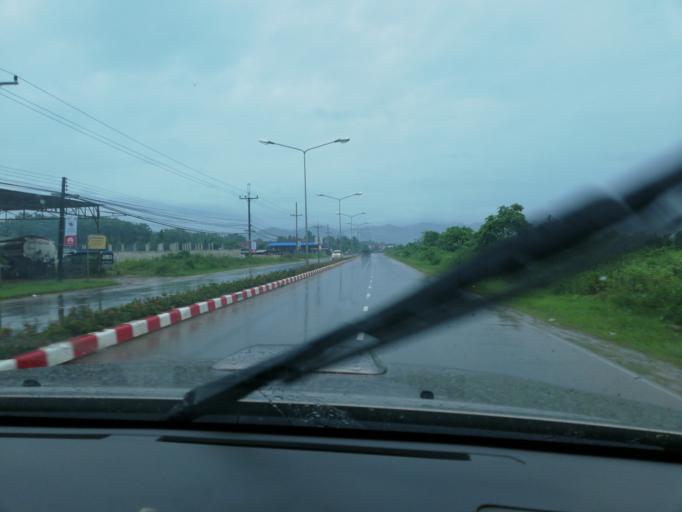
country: LA
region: Loungnamtha
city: Louang Namtha
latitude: 20.9586
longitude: 101.4039
